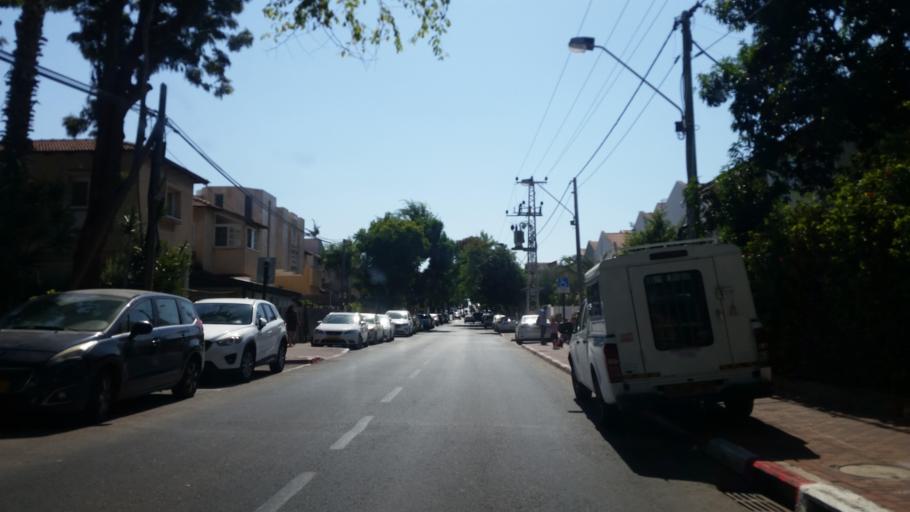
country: IL
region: Central District
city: Ra'anana
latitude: 32.1830
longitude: 34.8858
